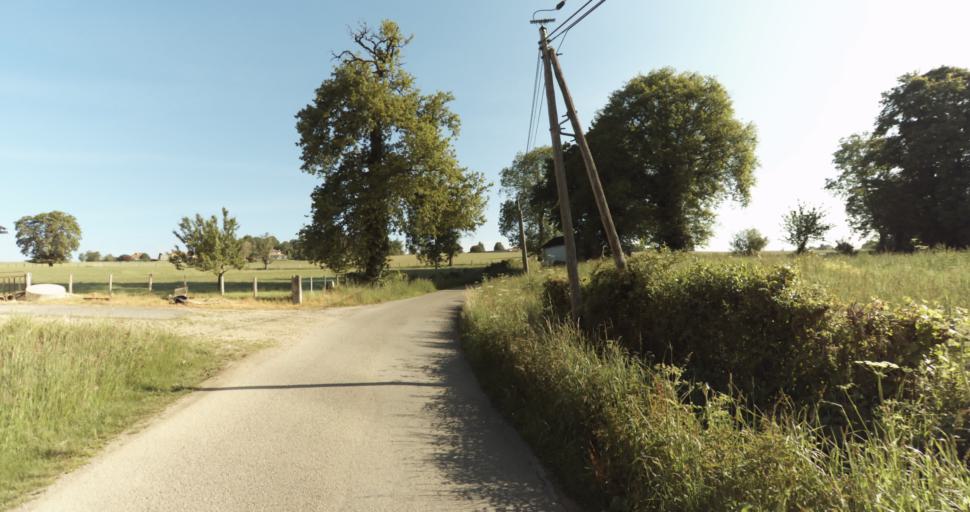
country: FR
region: Limousin
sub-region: Departement de la Haute-Vienne
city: Solignac
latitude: 45.7398
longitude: 1.2714
